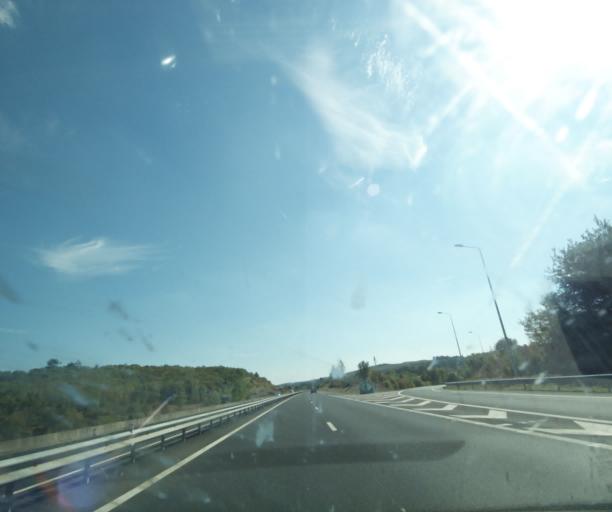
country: FR
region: Limousin
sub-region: Departement de la Correze
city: Brive-la-Gaillarde
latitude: 45.0362
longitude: 1.5250
